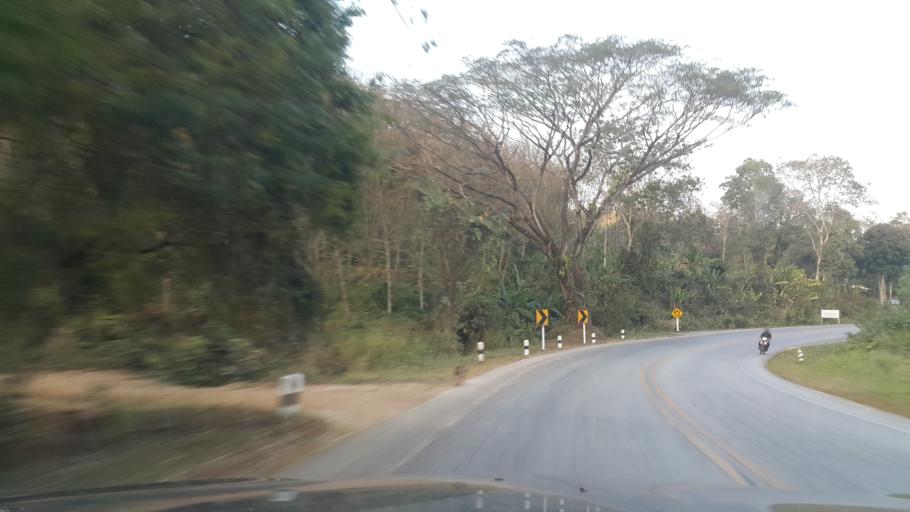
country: TH
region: Loei
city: Loei
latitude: 17.4835
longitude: 101.6082
